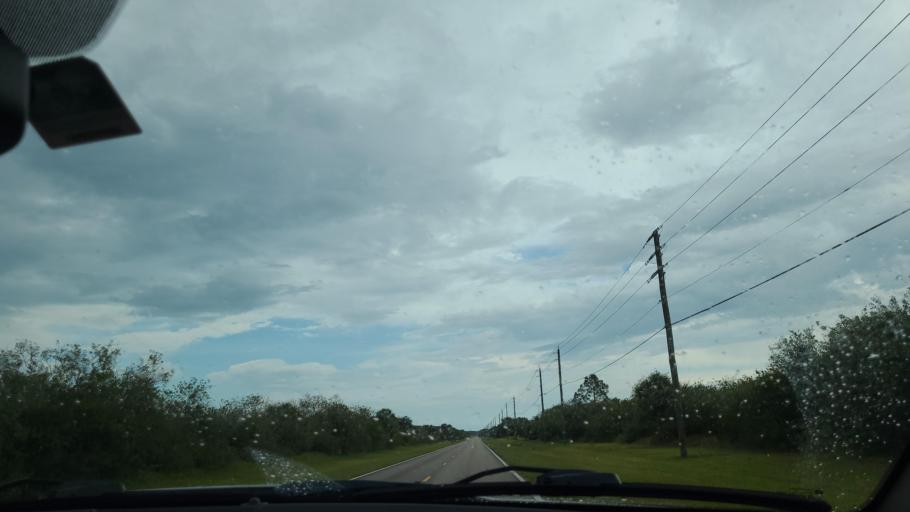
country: US
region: Florida
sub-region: Brevard County
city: June Park
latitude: 27.9529
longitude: -80.7003
